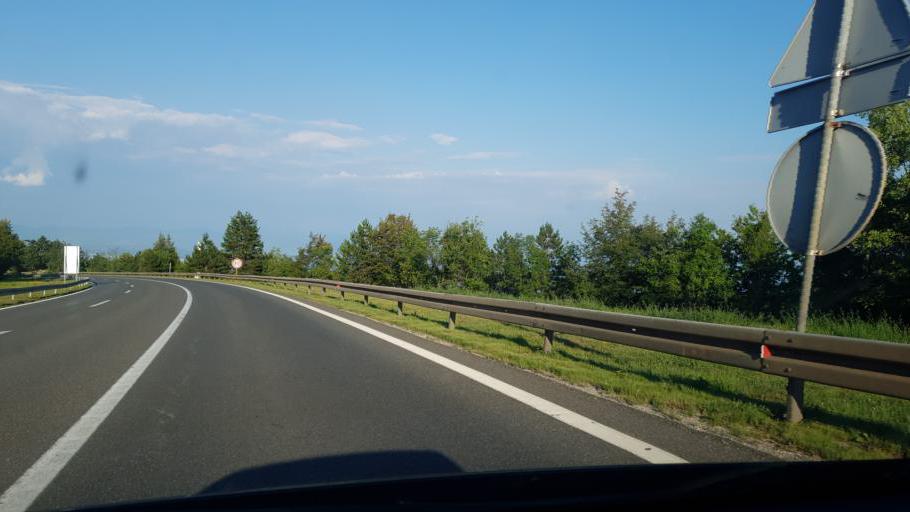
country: HR
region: Istarska
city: Lovran
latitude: 45.3141
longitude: 14.2509
